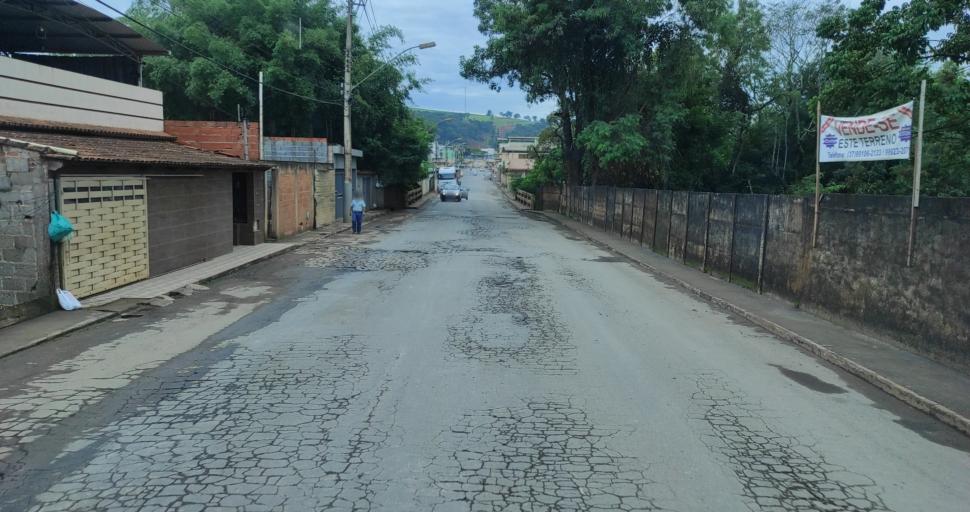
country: BR
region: Minas Gerais
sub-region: Arcos
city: Arcos
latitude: -20.3753
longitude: -45.6644
